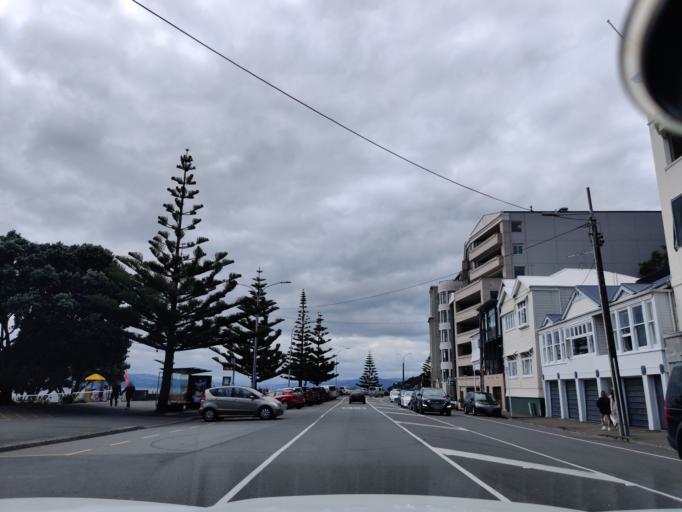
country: NZ
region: Wellington
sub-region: Wellington City
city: Wellington
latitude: -41.2912
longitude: 174.7899
